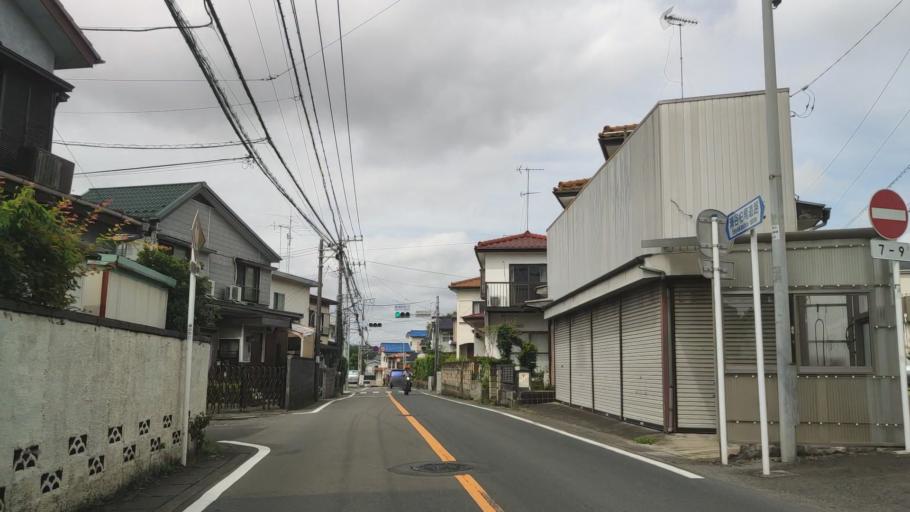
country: JP
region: Kanagawa
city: Minami-rinkan
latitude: 35.4854
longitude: 139.4741
